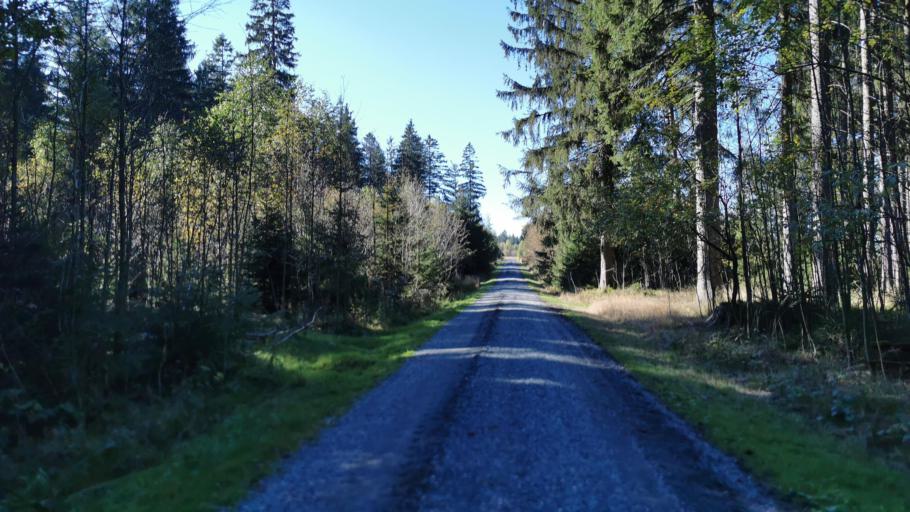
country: DE
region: Bavaria
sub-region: Upper Franconia
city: Tettau
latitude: 50.4780
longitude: 11.2746
